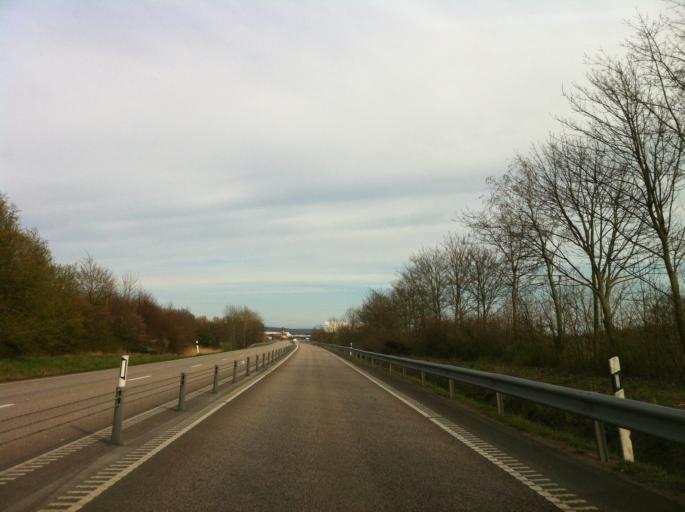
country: SE
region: Skane
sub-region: Bjuvs Kommun
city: Bjuv
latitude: 56.0739
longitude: 12.9197
